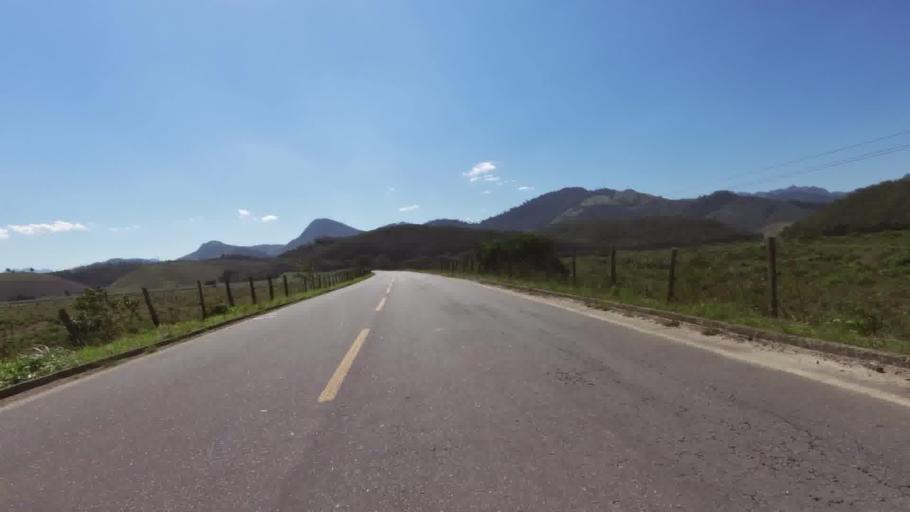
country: BR
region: Espirito Santo
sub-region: Rio Novo Do Sul
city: Rio Novo do Sul
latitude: -20.8873
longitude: -40.9016
